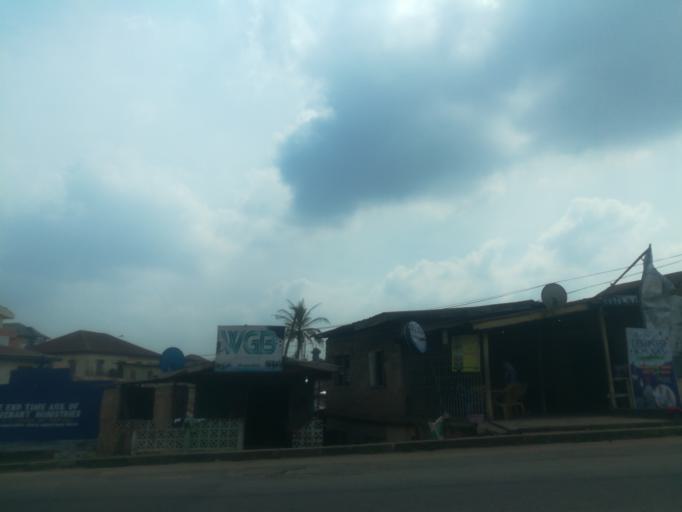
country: NG
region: Oyo
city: Ibadan
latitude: 7.3873
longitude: 3.8996
